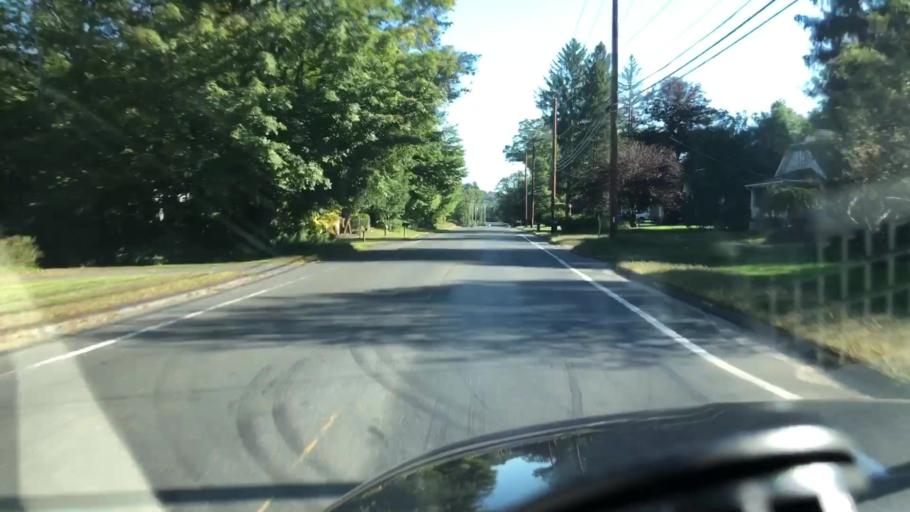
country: US
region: Massachusetts
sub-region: Hampden County
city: Palmer
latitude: 42.1372
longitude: -72.3096
